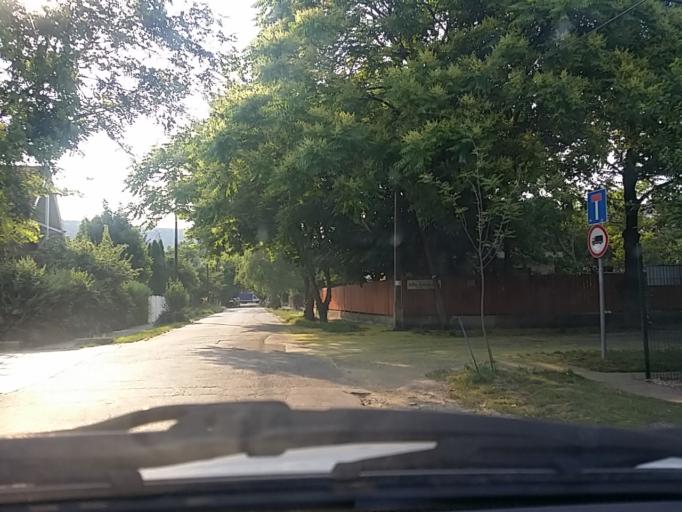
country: HU
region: Pest
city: Budakalasz
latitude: 47.5922
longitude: 19.0487
